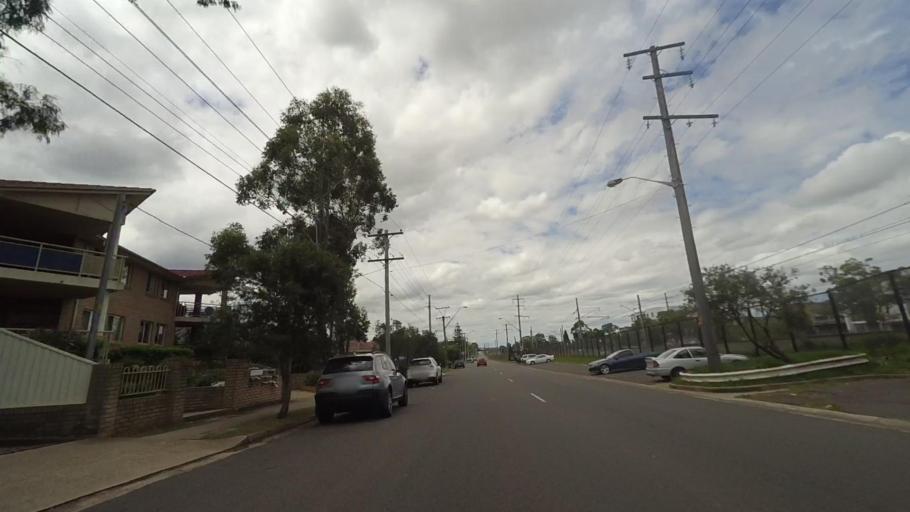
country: AU
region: New South Wales
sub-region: Holroyd
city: Guildford West
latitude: -33.8525
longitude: 150.9855
